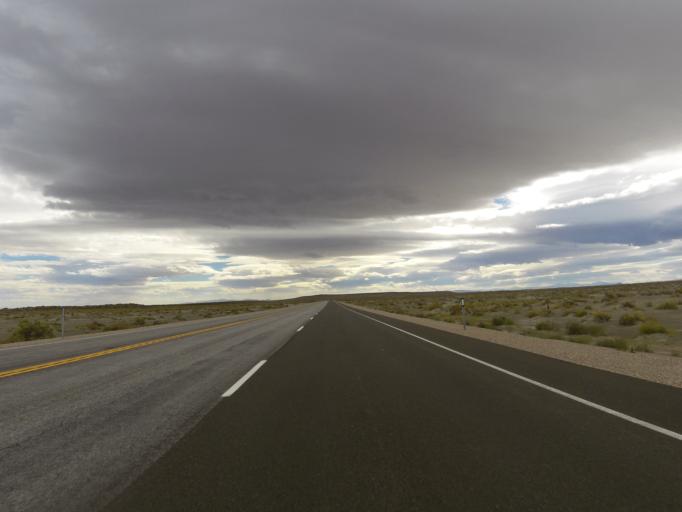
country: US
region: Nevada
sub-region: Churchill County
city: Fallon
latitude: 39.6941
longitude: -118.7754
